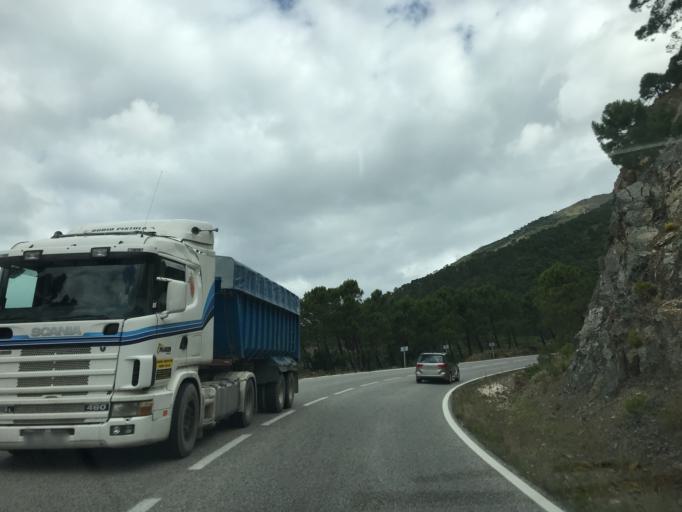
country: ES
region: Andalusia
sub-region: Provincia de Malaga
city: Benahavis
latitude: 36.5651
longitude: -5.0594
